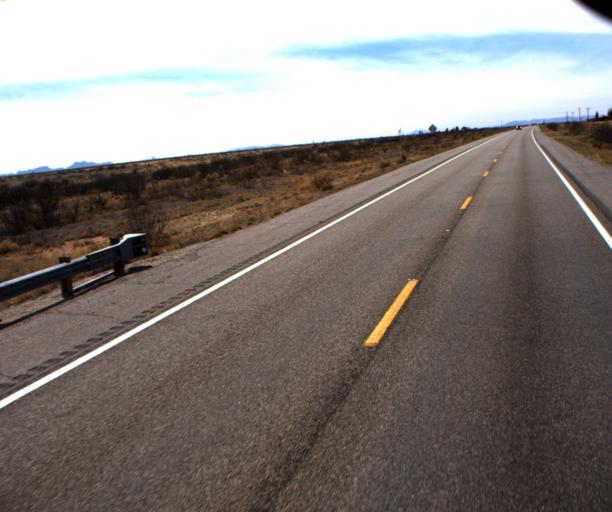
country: US
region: Arizona
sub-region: Cochise County
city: Pirtleville
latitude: 31.5931
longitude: -109.6695
